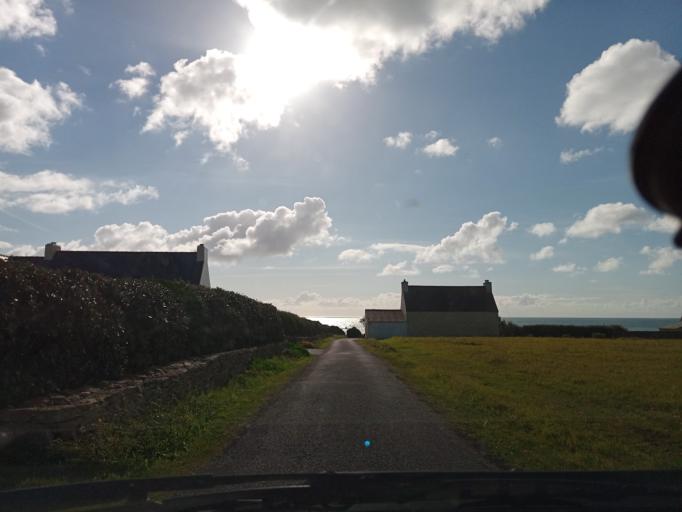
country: FR
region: Brittany
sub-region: Departement du Finistere
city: Plozevet
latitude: 47.9748
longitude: -4.4425
